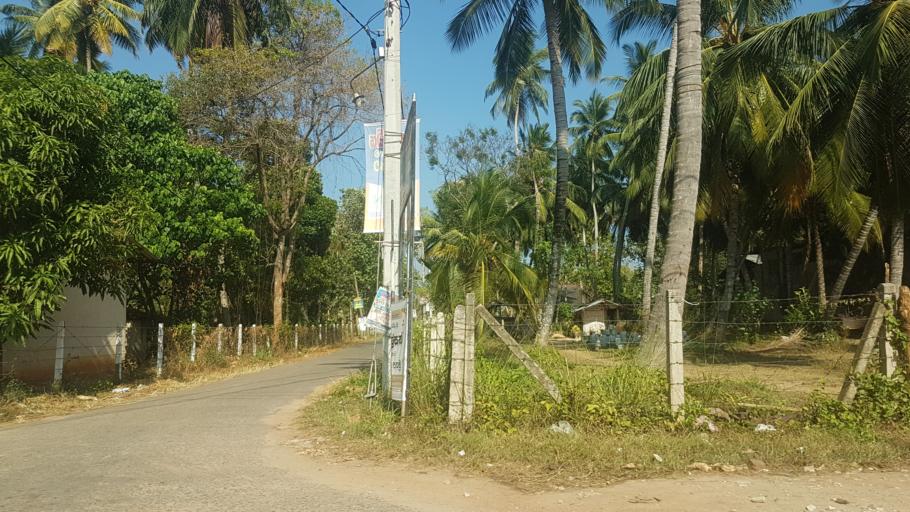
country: LK
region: North Western
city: Chilaw
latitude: 7.4059
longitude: 79.8315
